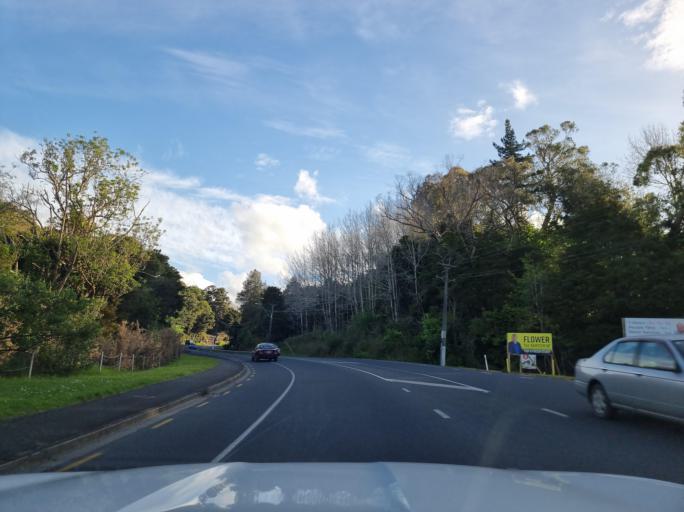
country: NZ
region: Northland
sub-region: Whangarei
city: Whangarei
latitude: -35.7359
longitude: 174.2857
